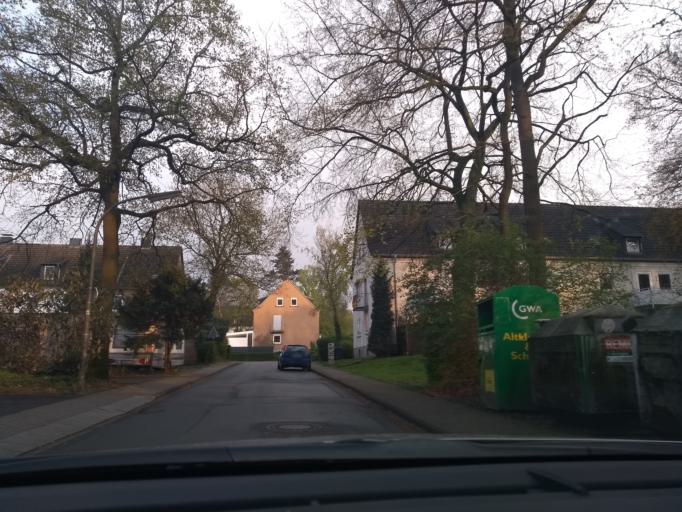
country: DE
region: North Rhine-Westphalia
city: Lunen
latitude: 51.6263
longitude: 7.4837
